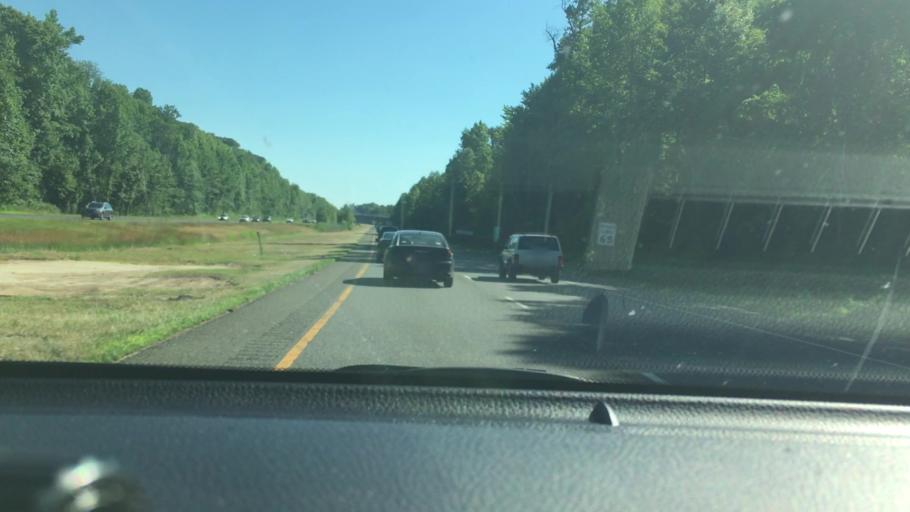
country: US
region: New Jersey
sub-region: Gloucester County
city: Pitman
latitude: 39.7512
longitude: -75.1388
